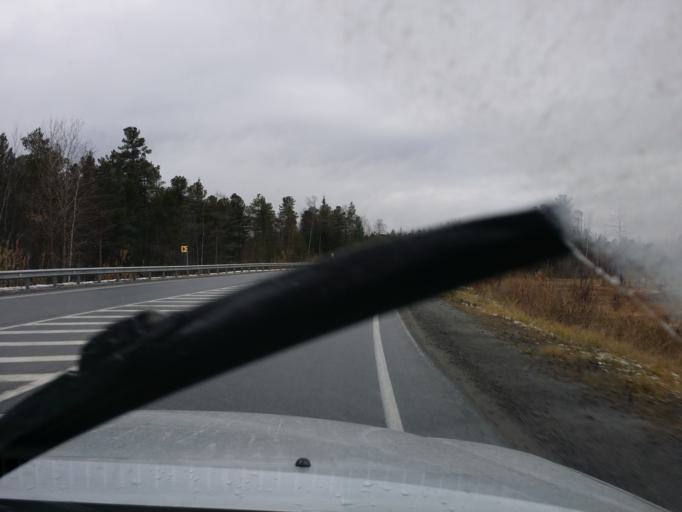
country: RU
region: Khanty-Mansiyskiy Avtonomnyy Okrug
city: Megion
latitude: 61.1005
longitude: 75.8596
